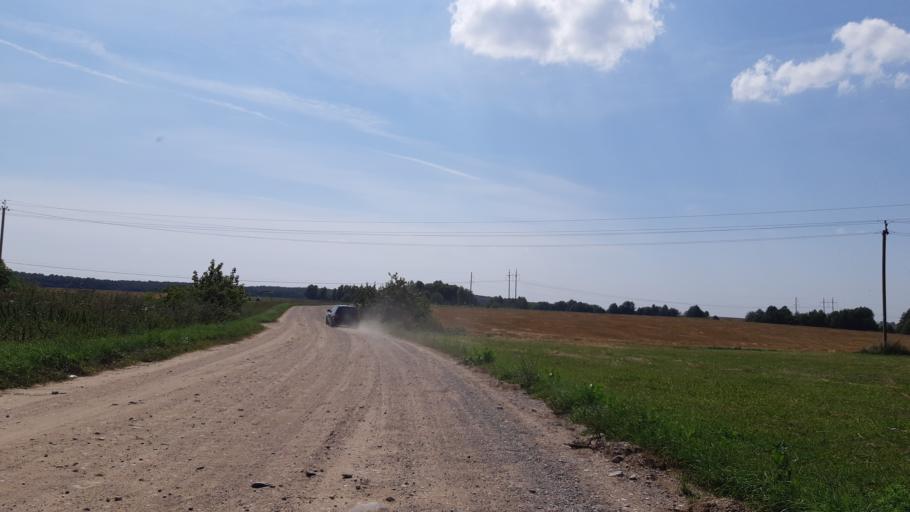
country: LT
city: Virbalis
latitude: 54.6222
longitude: 22.8084
